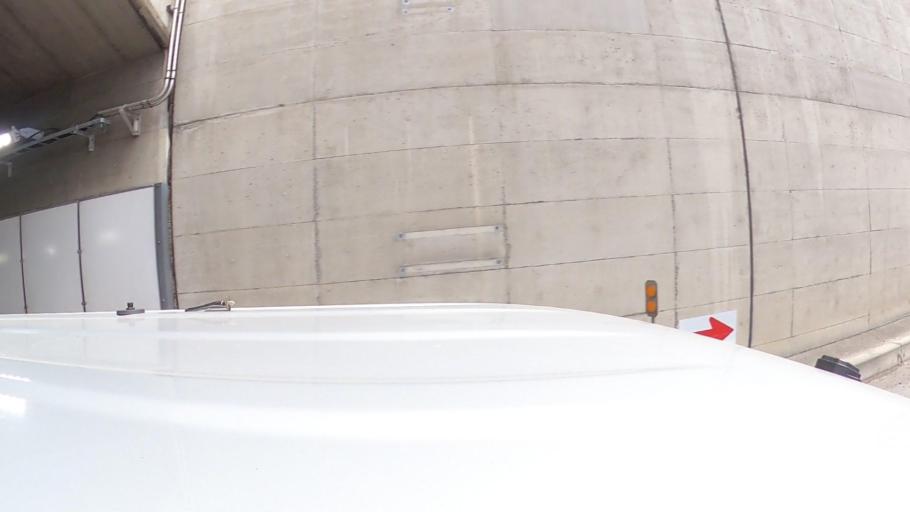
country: JP
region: Saitama
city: Wako
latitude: 35.7980
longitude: 139.6174
